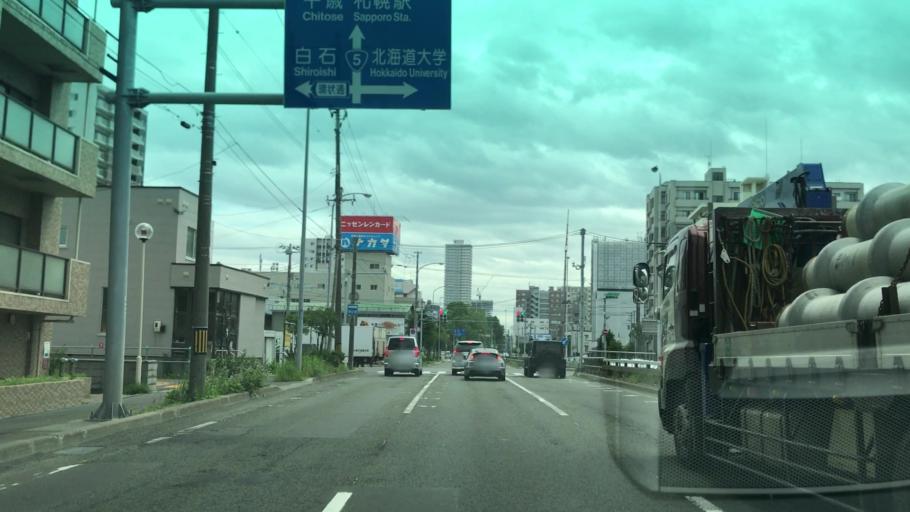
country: JP
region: Hokkaido
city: Sapporo
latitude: 43.0795
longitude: 141.3519
